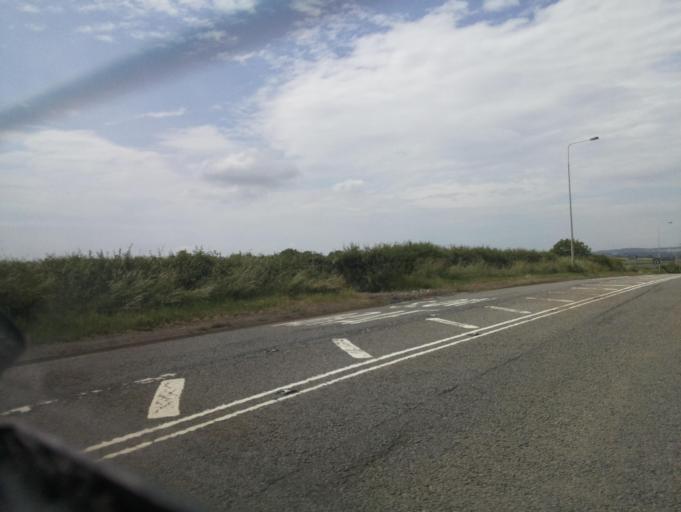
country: GB
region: Wales
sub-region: Vale of Glamorgan
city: Llangan
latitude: 51.4776
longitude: -3.5158
